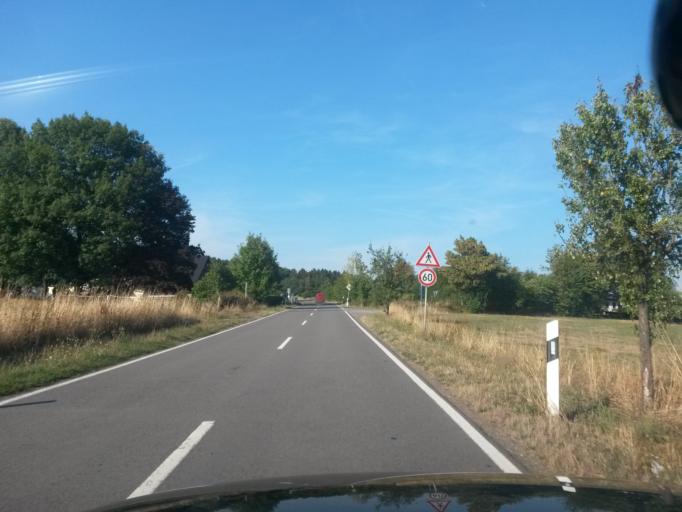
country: DE
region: North Rhine-Westphalia
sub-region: Regierungsbezirk Koln
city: Ruppichteroth
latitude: 50.8539
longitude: 7.4825
